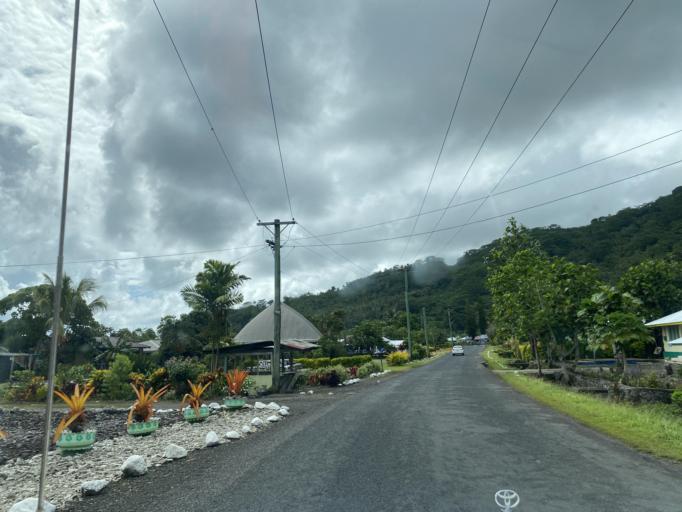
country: WS
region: Atua
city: Solosolo
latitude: -13.8734
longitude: -171.6419
